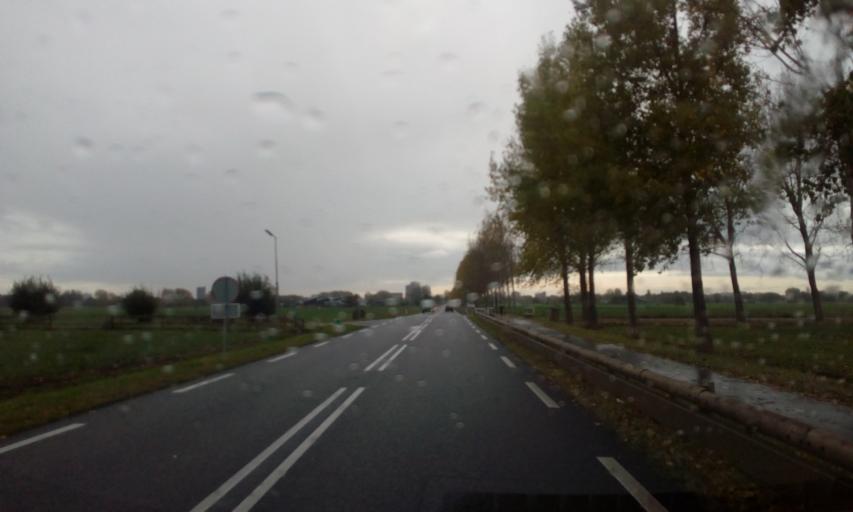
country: NL
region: South Holland
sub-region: Gemeente Zoetermeer
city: Zoetermeer
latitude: 52.0821
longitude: 4.4756
